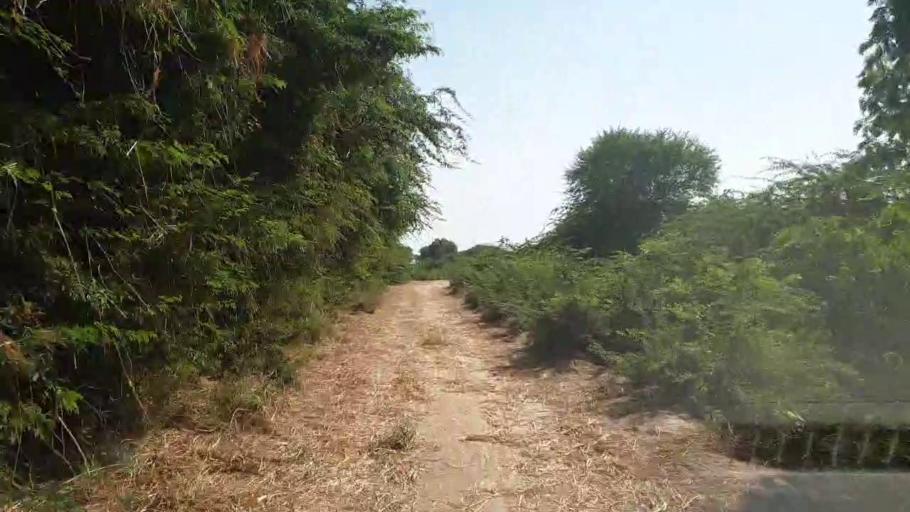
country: PK
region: Sindh
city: Kadhan
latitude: 24.6339
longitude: 68.9929
